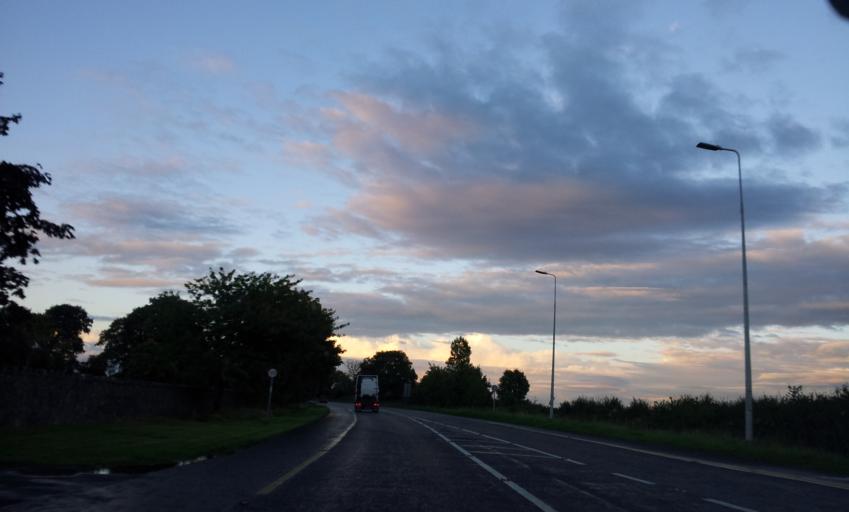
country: IE
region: Munster
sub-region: County Limerick
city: Rathkeale
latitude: 52.5359
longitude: -8.8653
